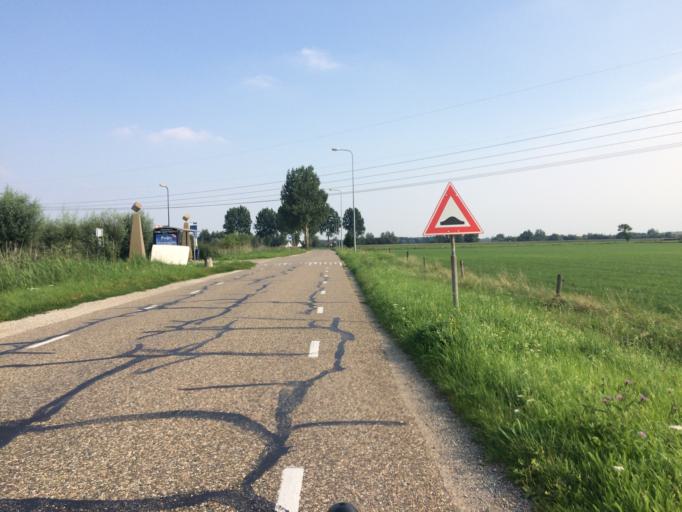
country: NL
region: Gelderland
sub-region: Gemeente Maasdriel
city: Hedel
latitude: 51.7214
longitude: 5.2418
